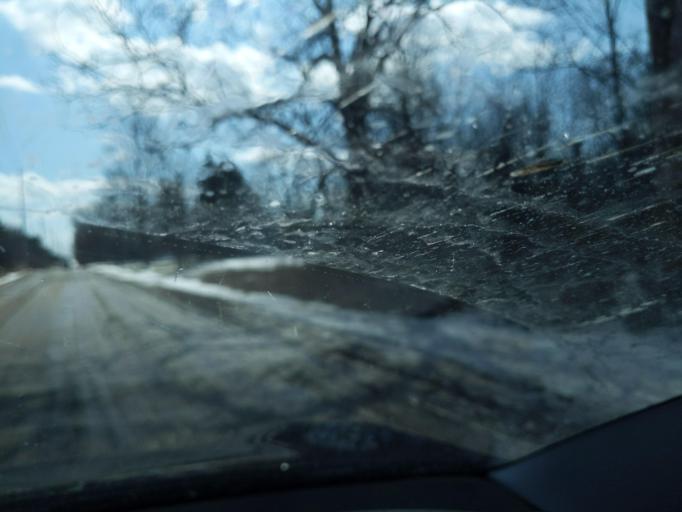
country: US
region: Michigan
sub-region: Livingston County
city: Fowlerville
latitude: 42.6278
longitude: -84.0914
